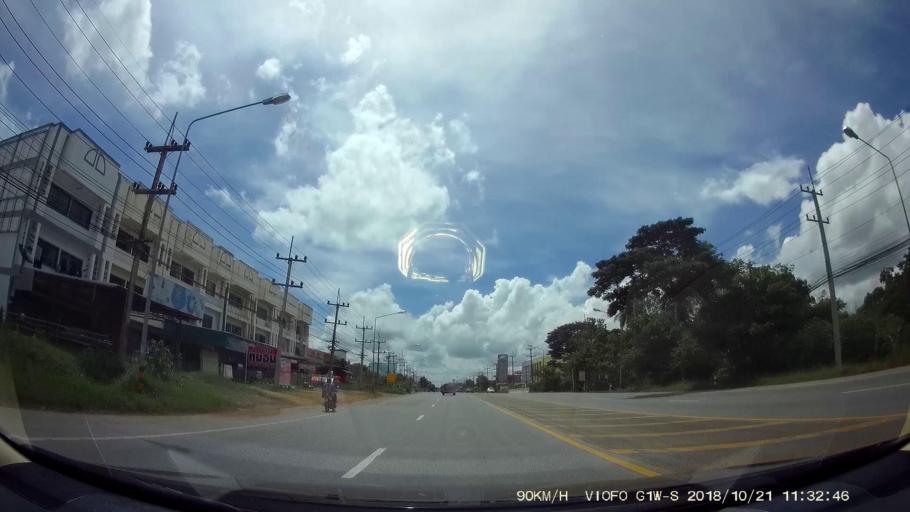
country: TH
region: Chaiyaphum
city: Chaiyaphum
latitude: 15.7540
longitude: 102.0240
